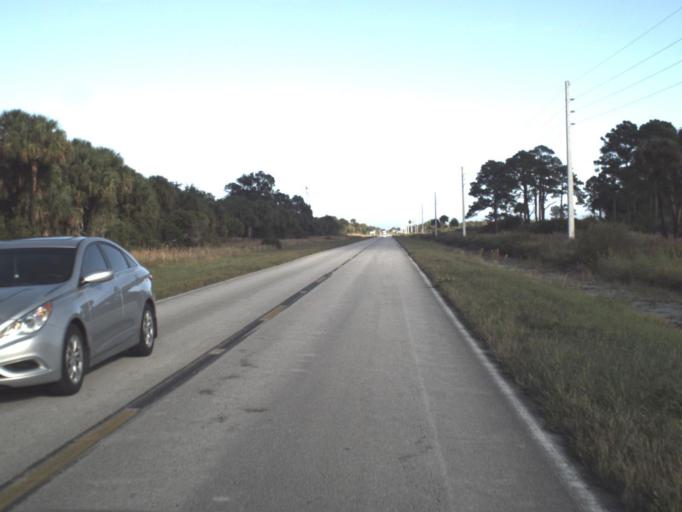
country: US
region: Florida
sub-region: Brevard County
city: Titusville
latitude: 28.6436
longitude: -80.7089
